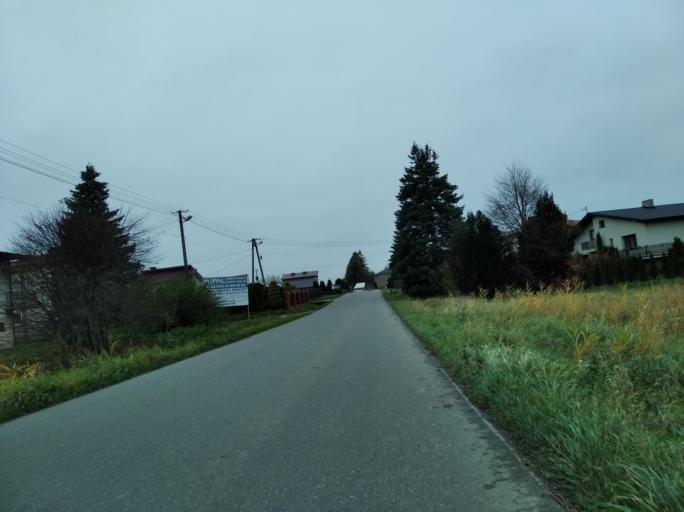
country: PL
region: Subcarpathian Voivodeship
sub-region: Powiat krosnienski
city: Jedlicze
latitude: 49.6855
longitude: 21.6703
